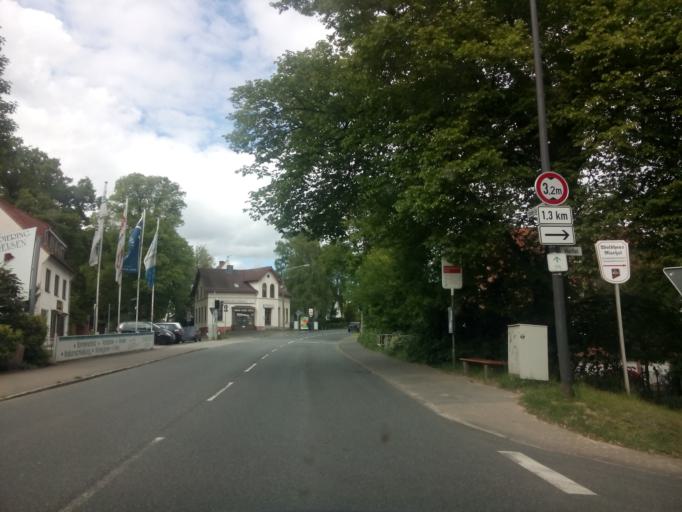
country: DE
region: Lower Saxony
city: Ritterhude
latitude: 53.1691
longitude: 8.7127
